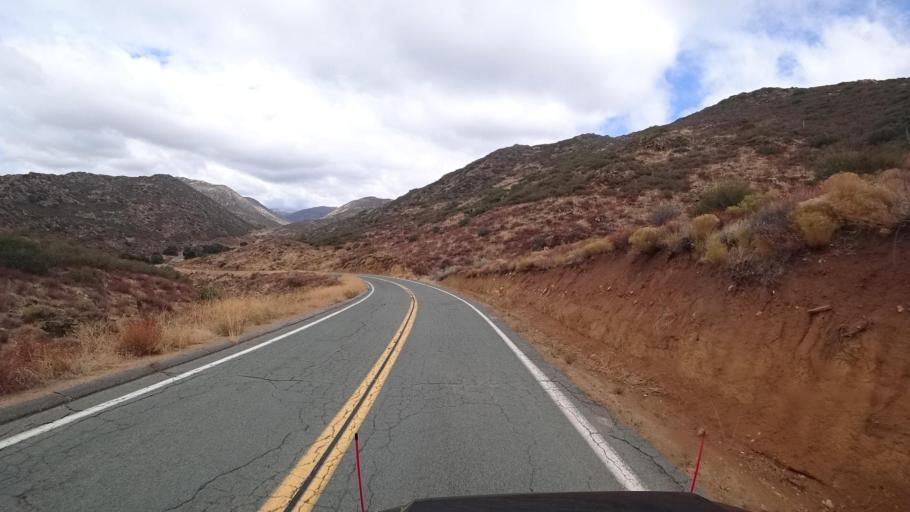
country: US
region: California
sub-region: San Diego County
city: Pine Valley
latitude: 32.7481
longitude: -116.4510
